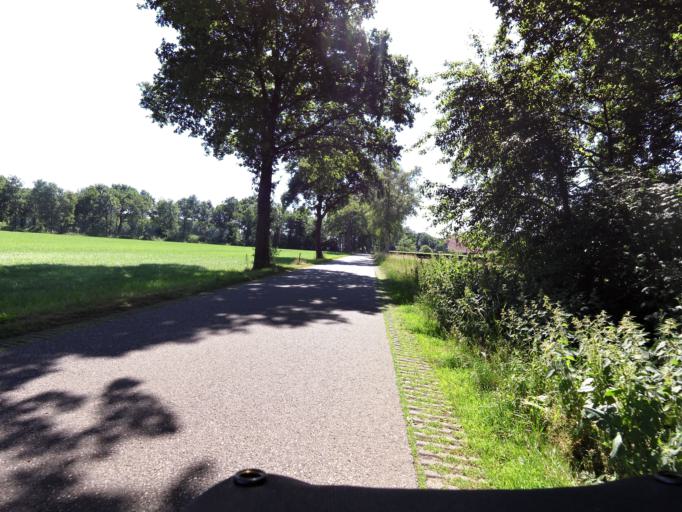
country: NL
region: Overijssel
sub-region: Gemeente Twenterand
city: Magele
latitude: 52.5317
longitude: 6.5026
